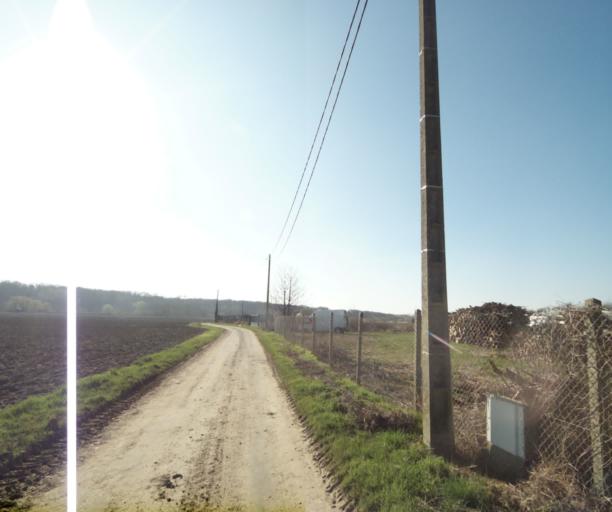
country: FR
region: Ile-de-France
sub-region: Departement du Val-d'Oise
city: Neuville-sur-Oise
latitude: 49.0222
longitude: 2.0787
